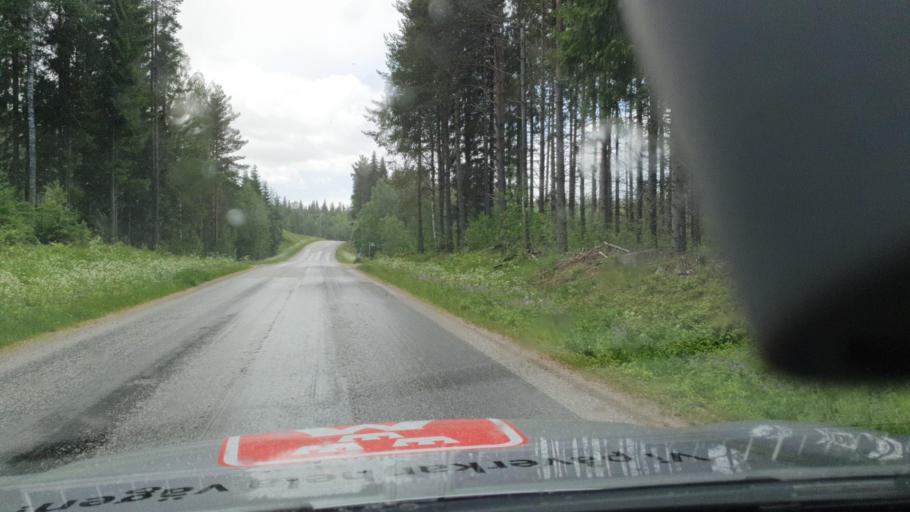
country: SE
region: Vaesternorrland
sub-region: OErnskoeldsviks Kommun
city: Bredbyn
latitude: 63.3317
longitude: 18.1112
